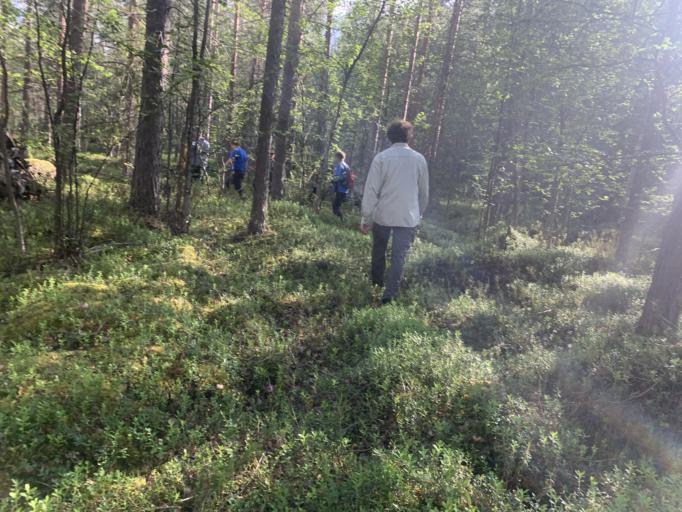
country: RU
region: Murmansk
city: Monchegorsk
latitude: 67.8797
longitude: 33.1048
